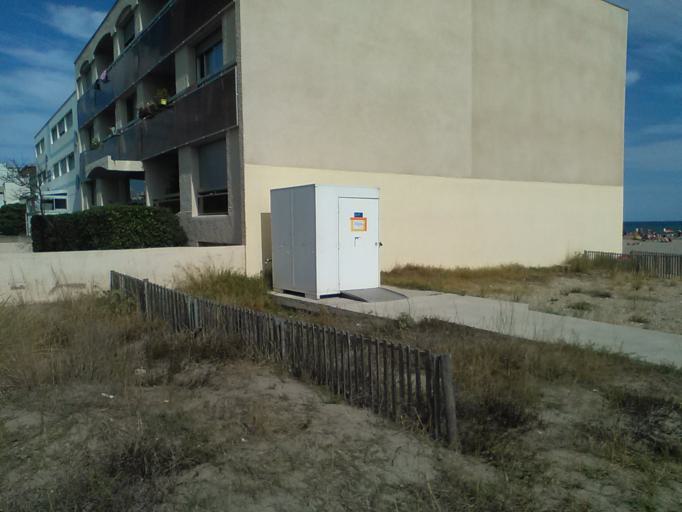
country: FR
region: Languedoc-Roussillon
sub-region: Departement de l'Herault
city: Perols
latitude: 43.5418
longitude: 3.9717
